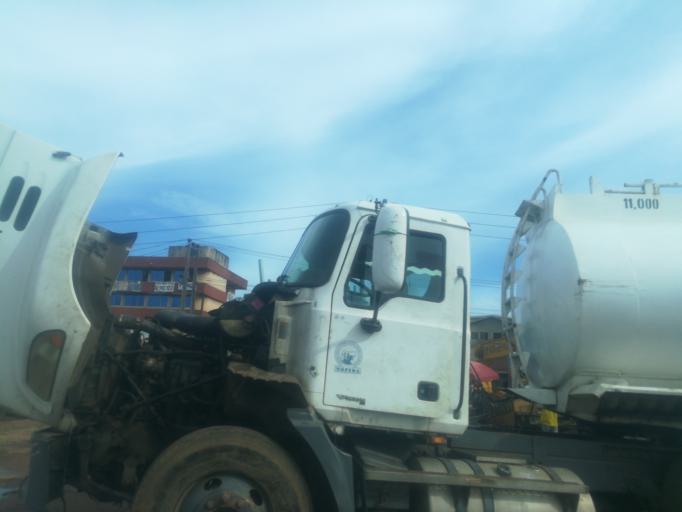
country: NG
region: Oyo
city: Ibadan
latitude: 7.3992
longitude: 3.9406
